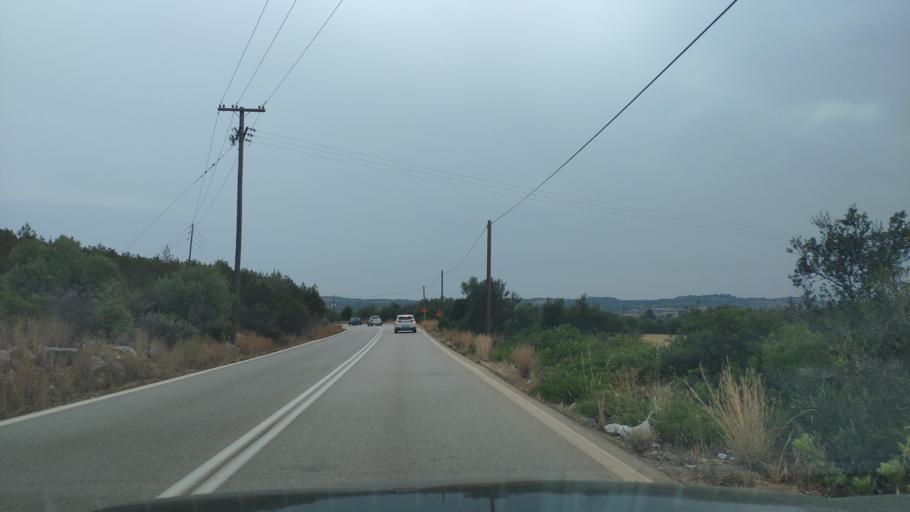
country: GR
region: Peloponnese
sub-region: Nomos Argolidos
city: Koilas
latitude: 37.4150
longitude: 23.1525
